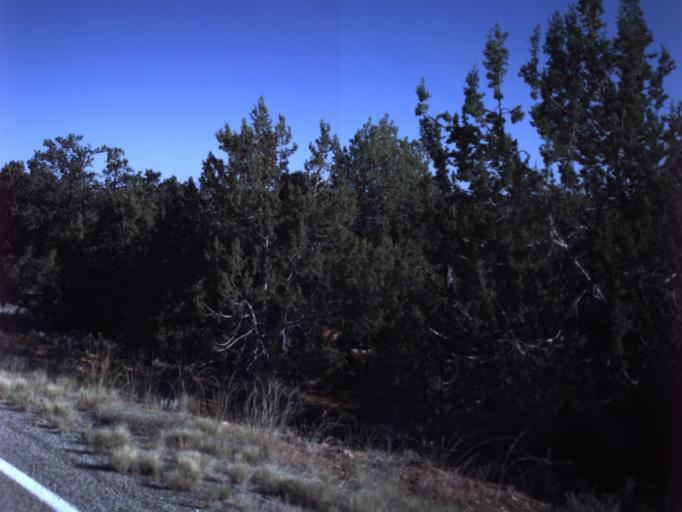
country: US
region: Utah
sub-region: San Juan County
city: Blanding
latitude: 37.5336
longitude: -109.7297
